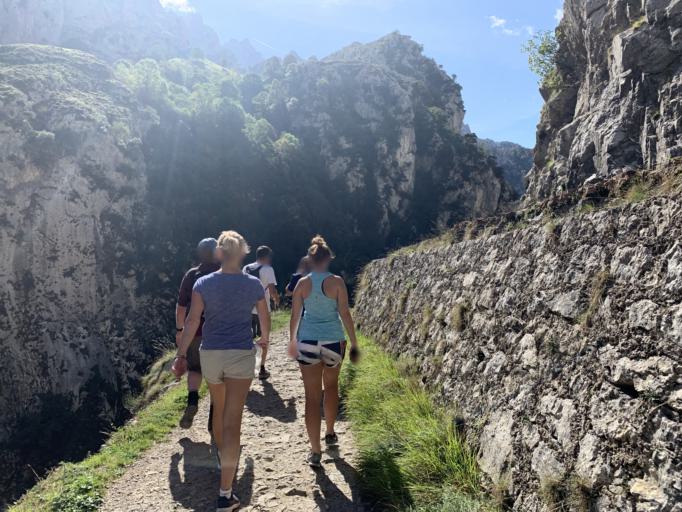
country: ES
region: Asturias
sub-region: Province of Asturias
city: Carrena
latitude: 43.2419
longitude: -4.8901
